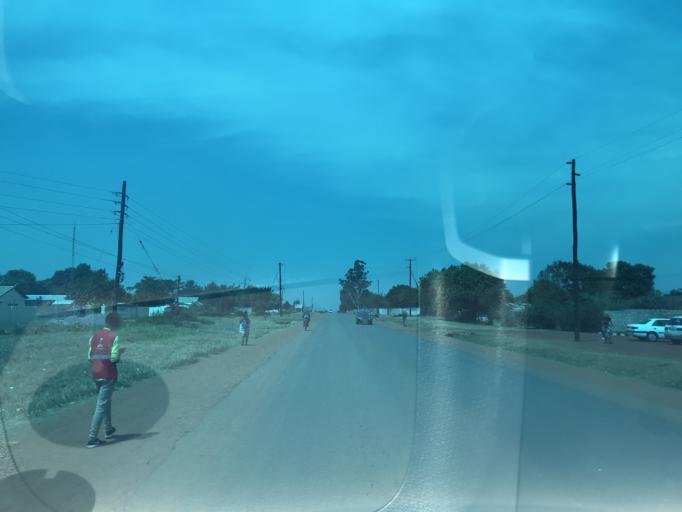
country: ZM
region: Northern
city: Kasama
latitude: -10.2054
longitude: 31.1792
